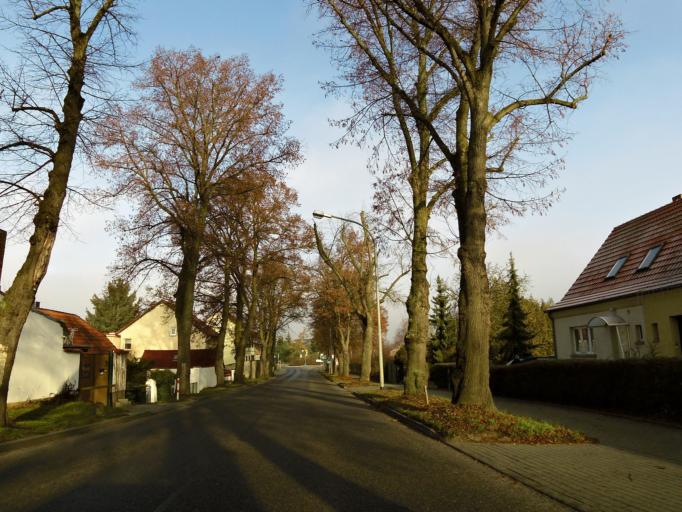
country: DE
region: Brandenburg
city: Werder
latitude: 52.3565
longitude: 12.9084
